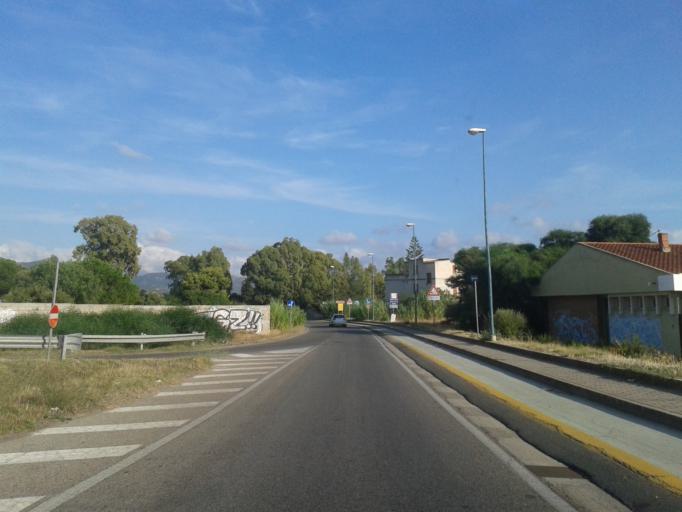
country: IT
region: Sardinia
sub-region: Provincia di Cagliari
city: Quartu Sant'Elena
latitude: 39.2181
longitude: 9.2852
